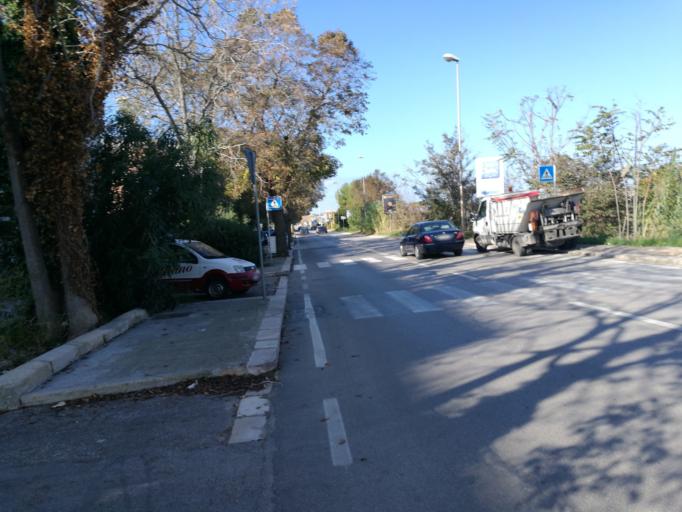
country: IT
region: Apulia
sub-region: Provincia di Bari
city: Triggiano
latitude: 41.1081
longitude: 16.9109
